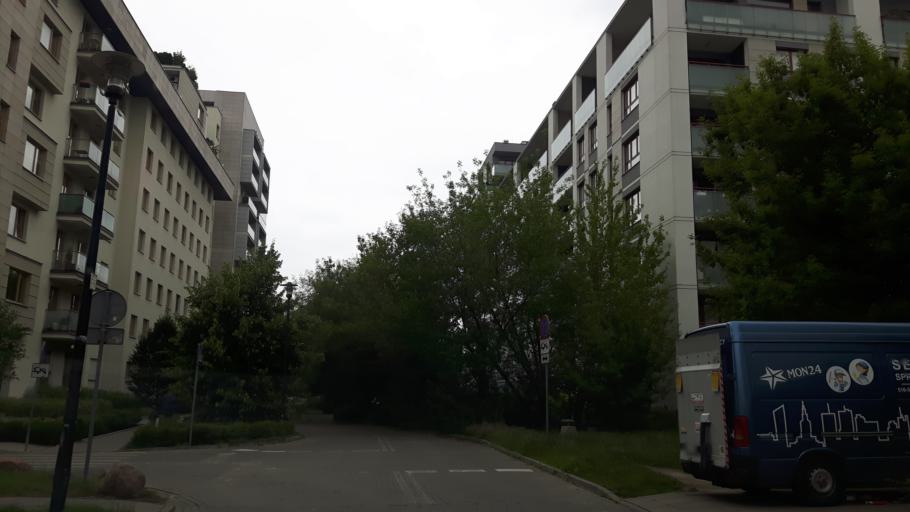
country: PL
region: Masovian Voivodeship
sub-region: Warszawa
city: Zoliborz
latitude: 52.2582
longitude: 20.9758
